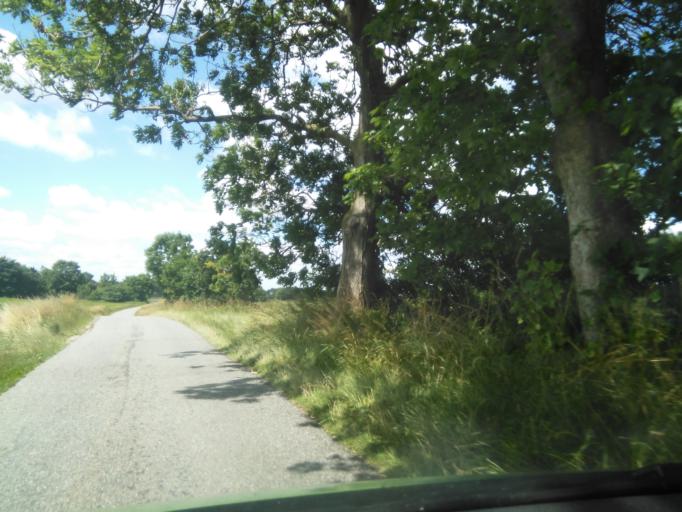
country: DK
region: Central Jutland
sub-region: Arhus Kommune
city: Logten
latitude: 56.1962
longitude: 10.3663
